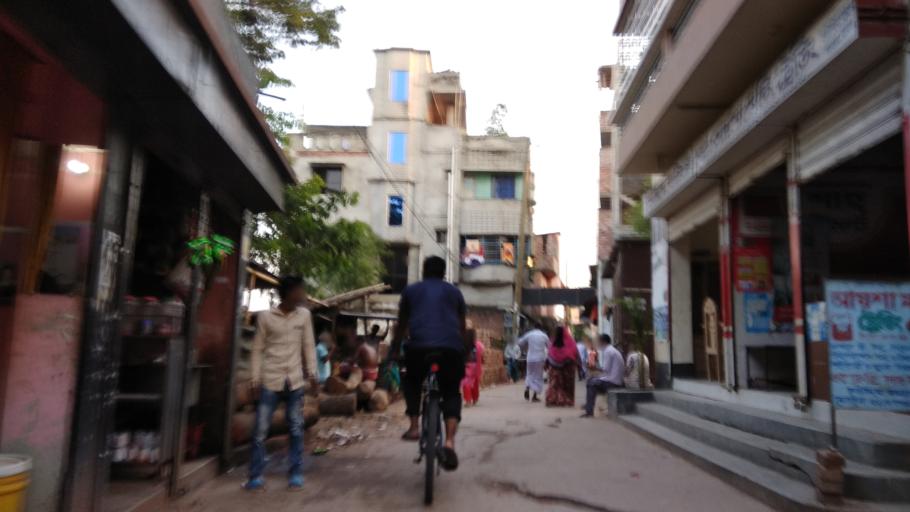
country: BD
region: Dhaka
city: Azimpur
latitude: 23.7990
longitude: 90.3388
